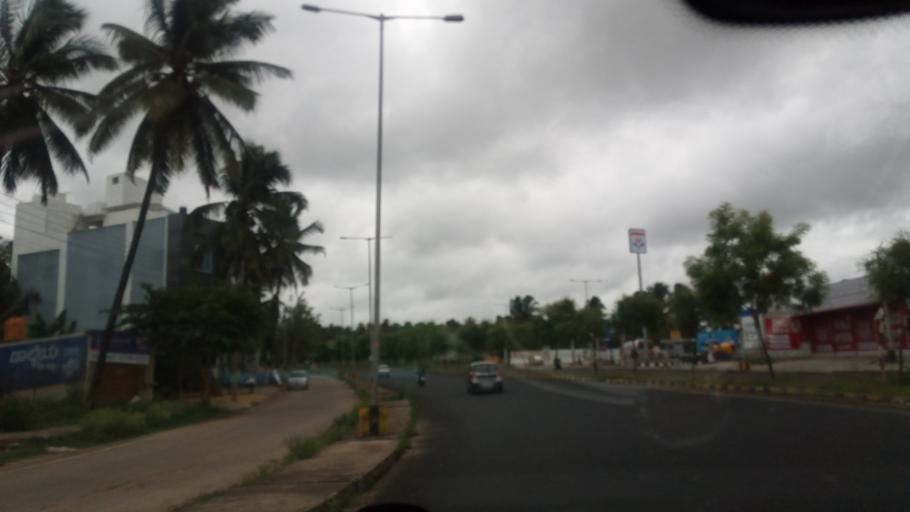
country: IN
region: Karnataka
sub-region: Mysore
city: Mysore
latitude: 12.3064
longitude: 76.6018
